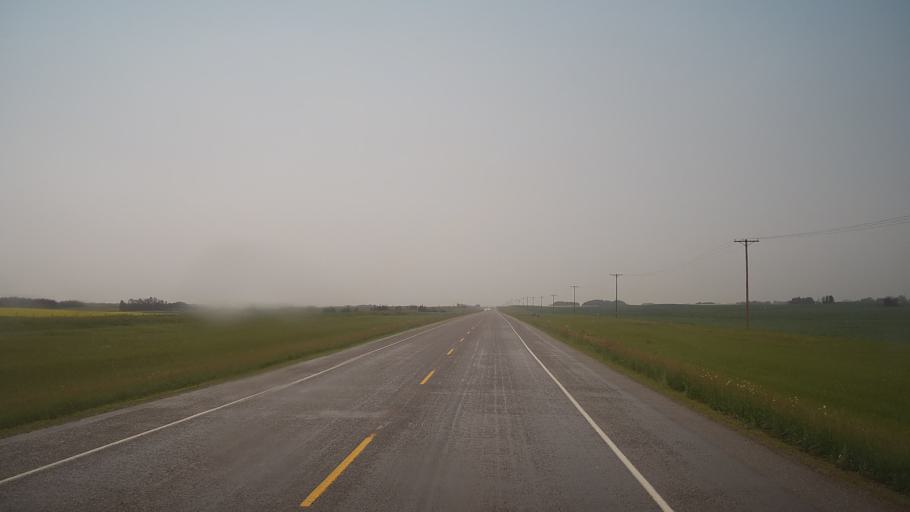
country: CA
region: Saskatchewan
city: Biggar
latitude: 52.1541
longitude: -108.2481
